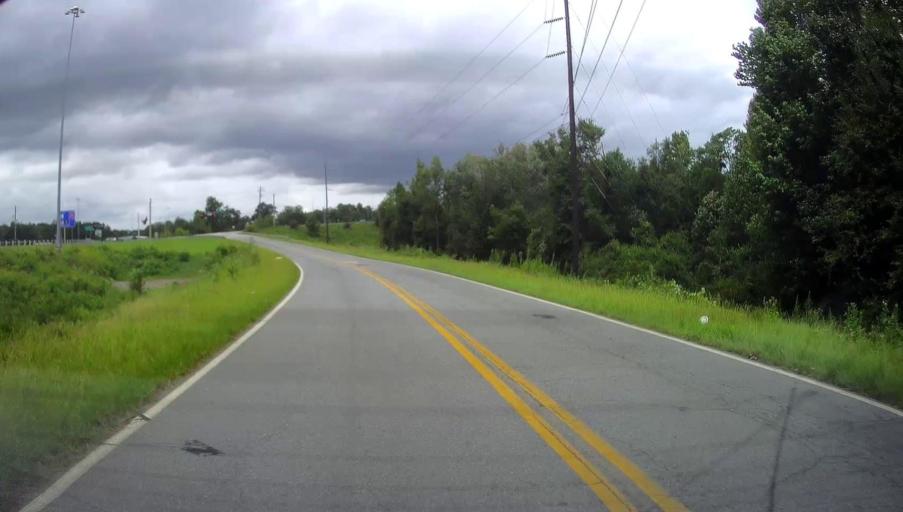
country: US
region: Georgia
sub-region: Bibb County
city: Macon
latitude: 32.8001
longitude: -83.5673
